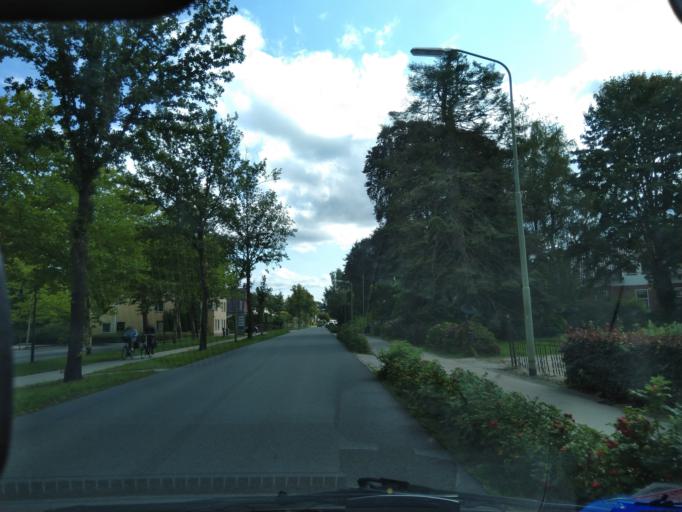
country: NL
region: Groningen
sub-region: Gemeente Haren
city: Haren
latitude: 53.1607
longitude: 6.5594
